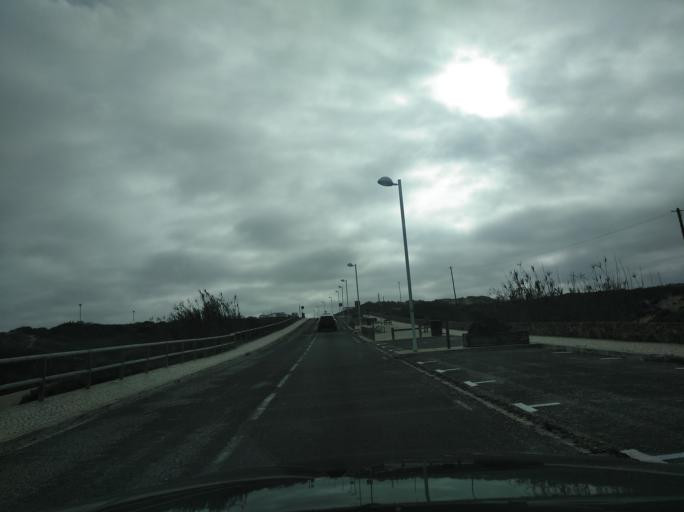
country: PT
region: Beja
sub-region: Odemira
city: Vila Nova de Milfontes
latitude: 37.7216
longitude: -8.7887
